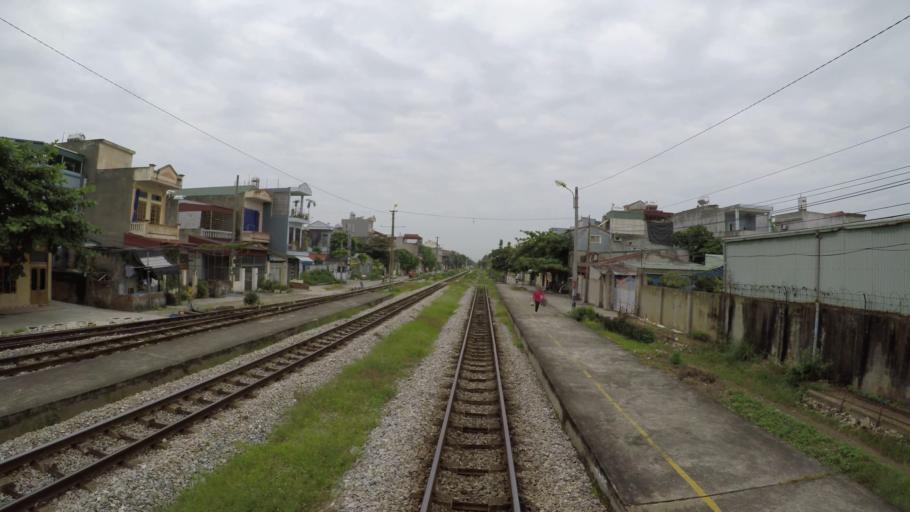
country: VN
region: Hai Duong
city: Thanh Pho Hai Duong
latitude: 20.9476
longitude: 106.3296
